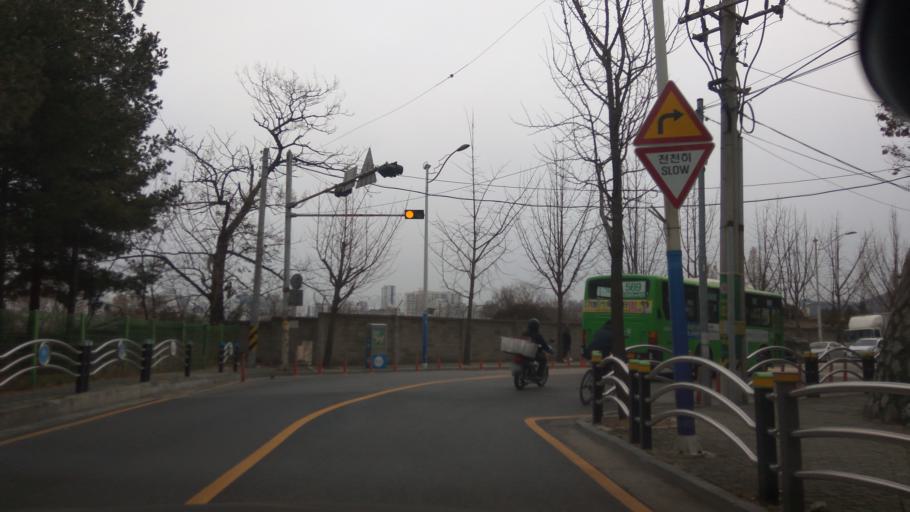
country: KR
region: Incheon
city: Incheon
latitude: 37.4940
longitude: 126.7096
